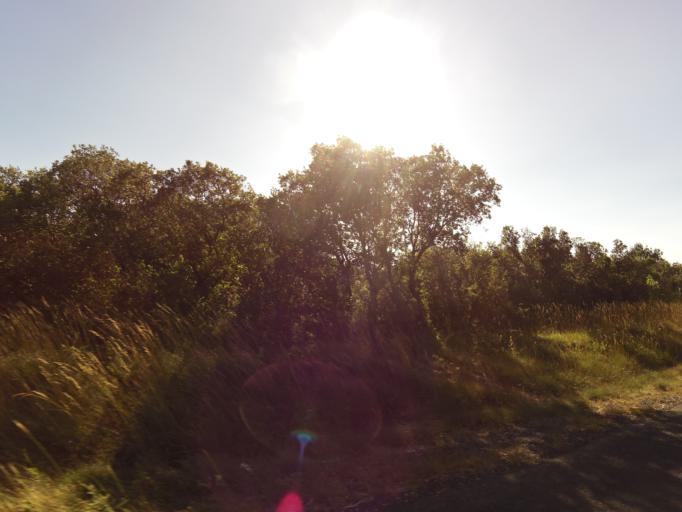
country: FR
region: Languedoc-Roussillon
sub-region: Departement du Gard
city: Aubais
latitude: 43.7510
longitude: 4.1227
